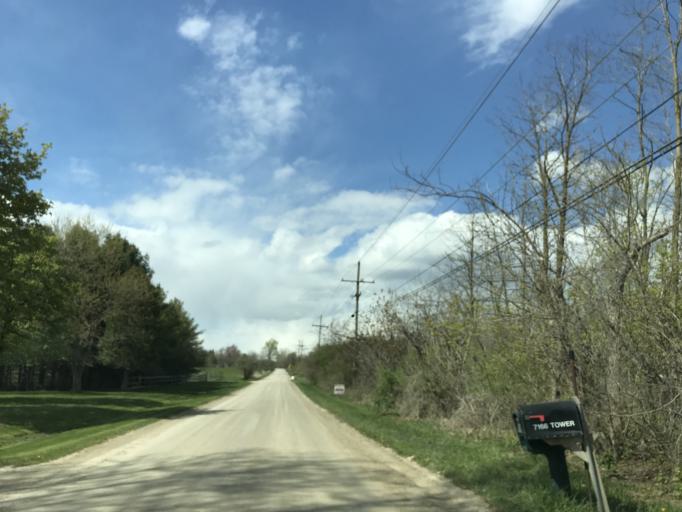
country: US
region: Michigan
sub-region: Oakland County
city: South Lyon
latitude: 42.3842
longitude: -83.6251
